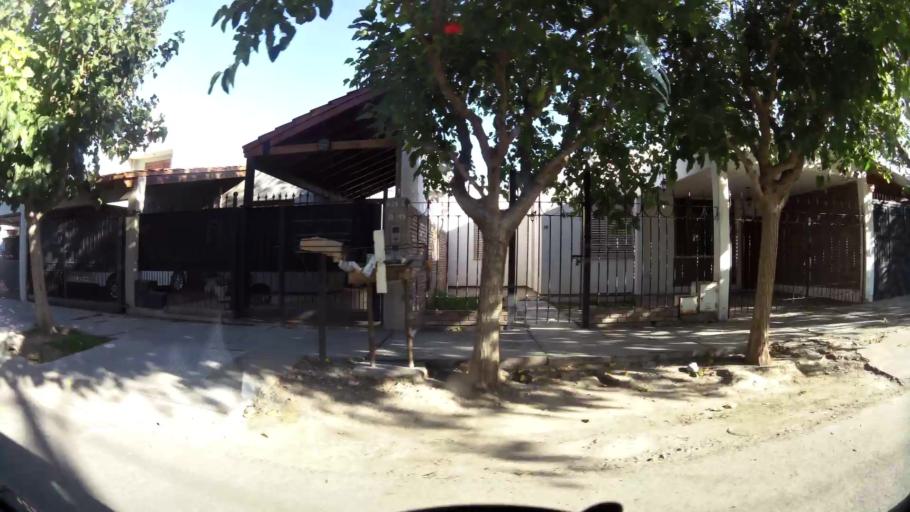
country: AR
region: San Juan
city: Villa Krause
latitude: -31.5596
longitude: -68.5168
